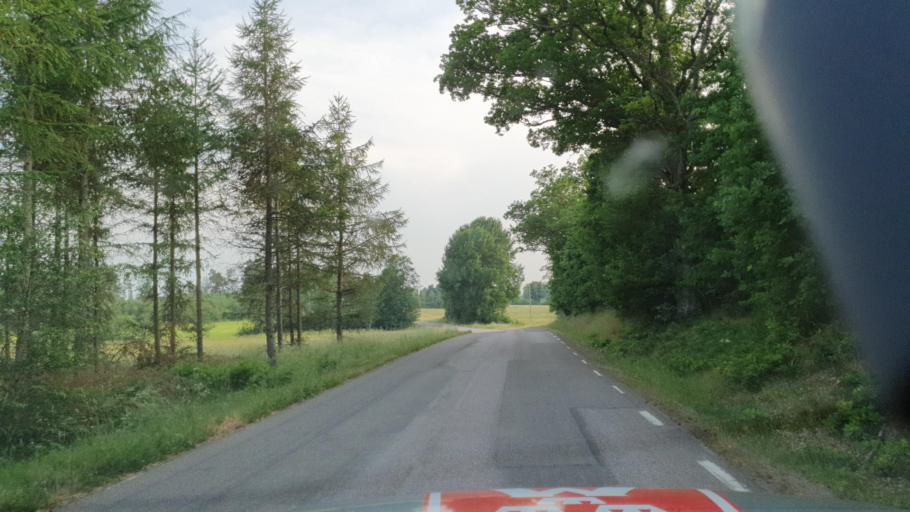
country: SE
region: Kalmar
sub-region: Torsas Kommun
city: Torsas
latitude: 56.4797
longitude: 16.0933
